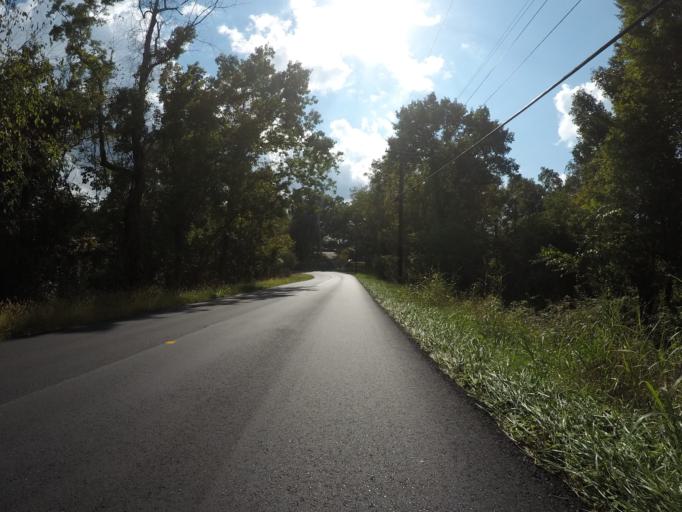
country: US
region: West Virginia
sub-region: Cabell County
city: Huntington
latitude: 38.3732
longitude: -82.4295
